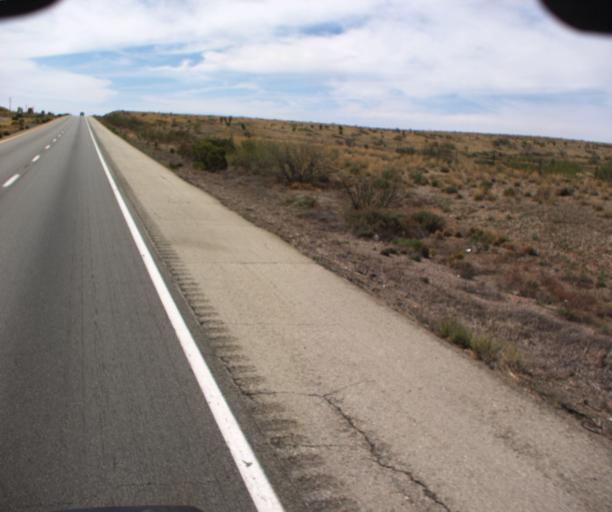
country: US
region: Arizona
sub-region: Cochise County
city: Willcox
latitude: 32.3537
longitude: -109.7153
